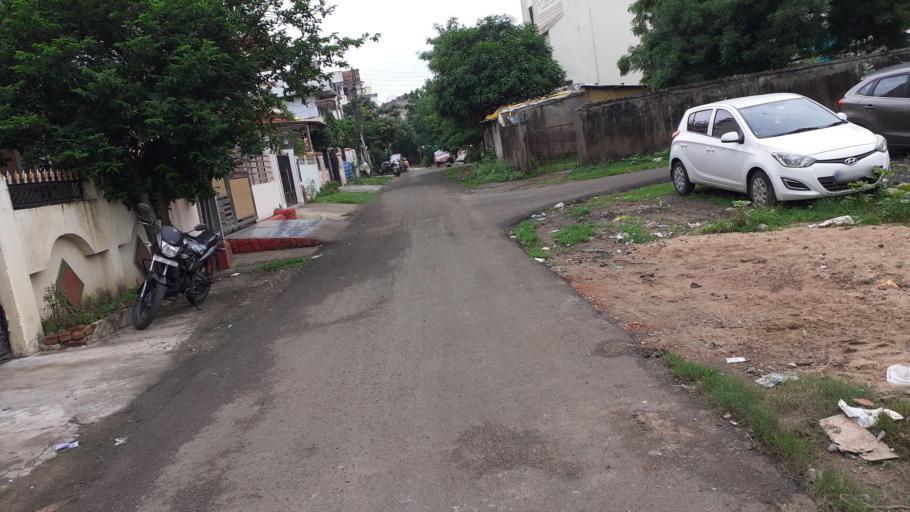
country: IN
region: Maharashtra
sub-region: Nagpur Division
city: Nagpur
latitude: 21.0970
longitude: 79.1139
